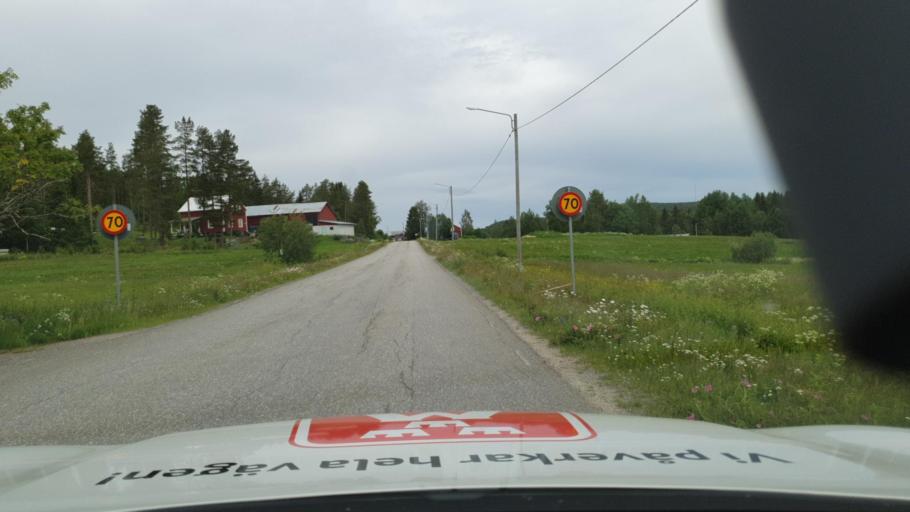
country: SE
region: Vaesterbotten
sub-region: Robertsfors Kommun
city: Robertsfors
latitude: 64.2478
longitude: 20.6601
